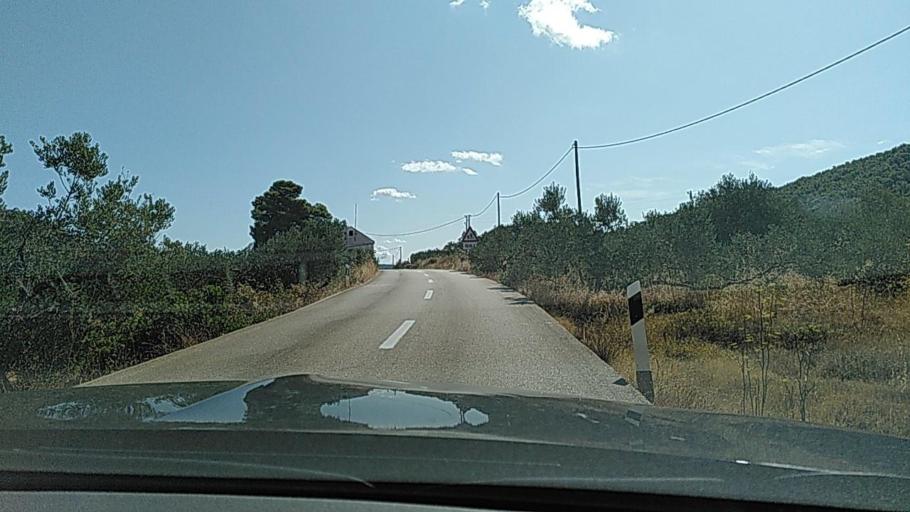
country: HR
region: Splitsko-Dalmatinska
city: Jelsa
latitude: 43.1444
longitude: 16.8390
